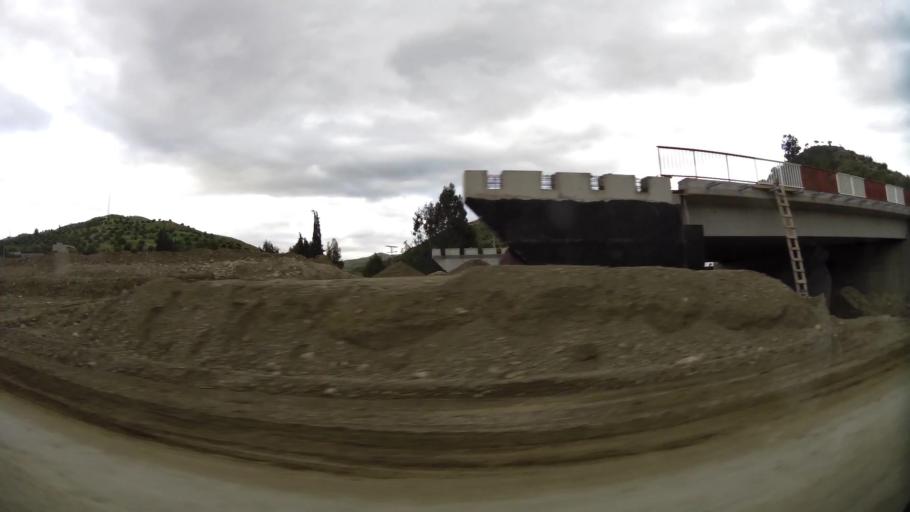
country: MA
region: Taza-Al Hoceima-Taounate
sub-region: Taza
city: Taza
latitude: 34.3492
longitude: -3.9219
